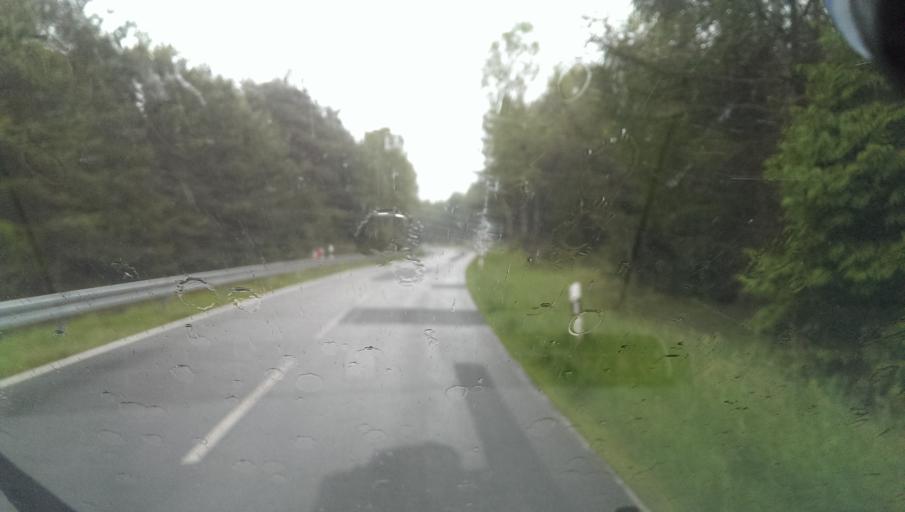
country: DE
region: Lower Saxony
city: Hermannsburg
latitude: 52.7899
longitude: 10.1483
